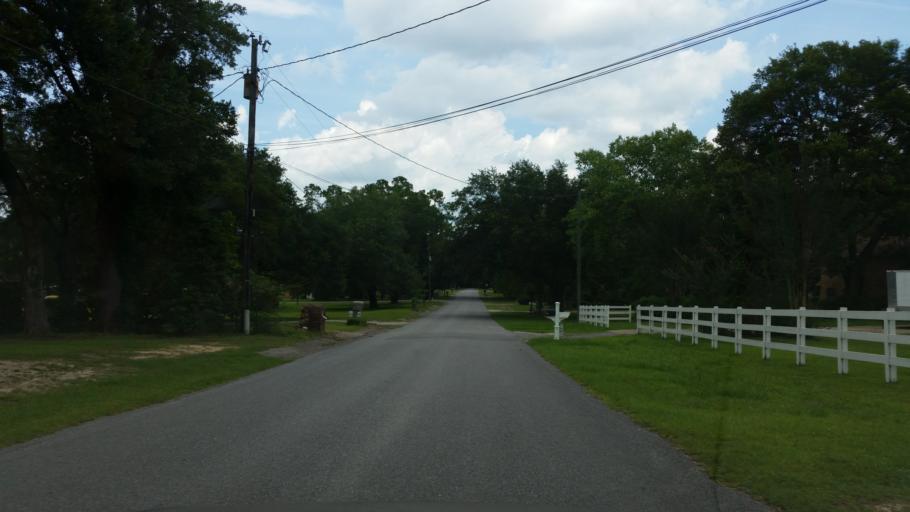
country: US
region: Florida
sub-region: Escambia County
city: Ensley
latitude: 30.5431
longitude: -87.3044
